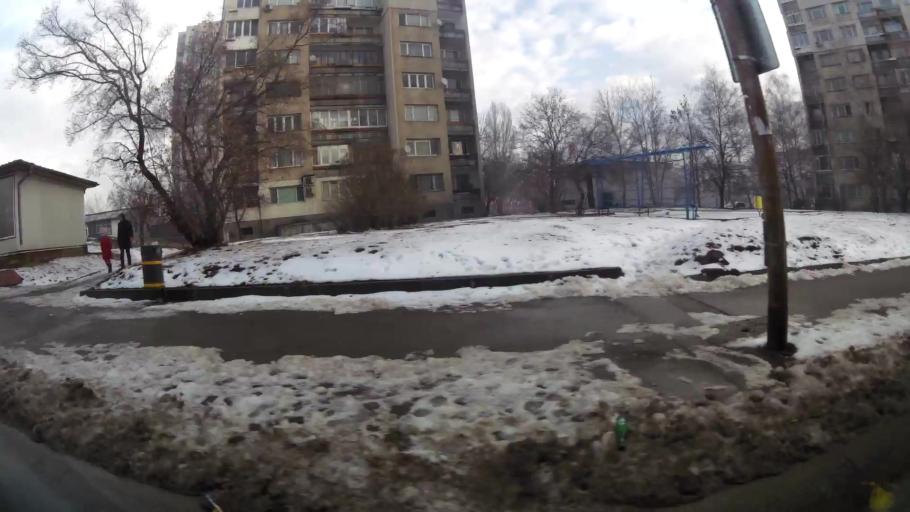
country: BG
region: Sofia-Capital
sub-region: Stolichna Obshtina
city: Sofia
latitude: 42.6973
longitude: 23.2774
